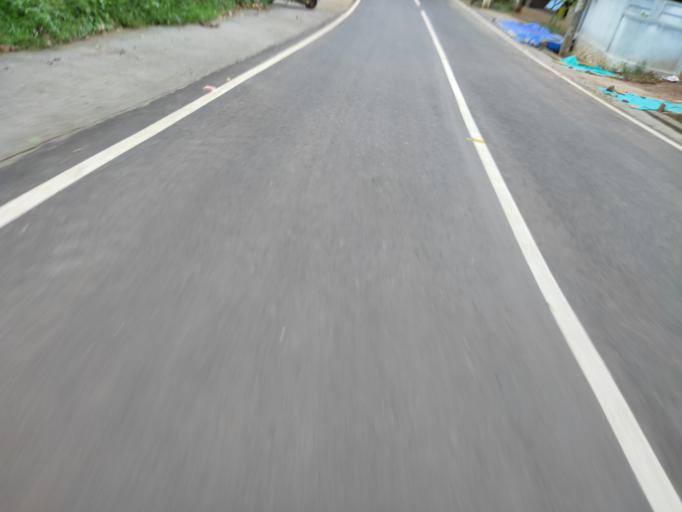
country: IN
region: Kerala
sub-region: Malappuram
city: Manjeri
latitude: 11.1866
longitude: 76.2121
